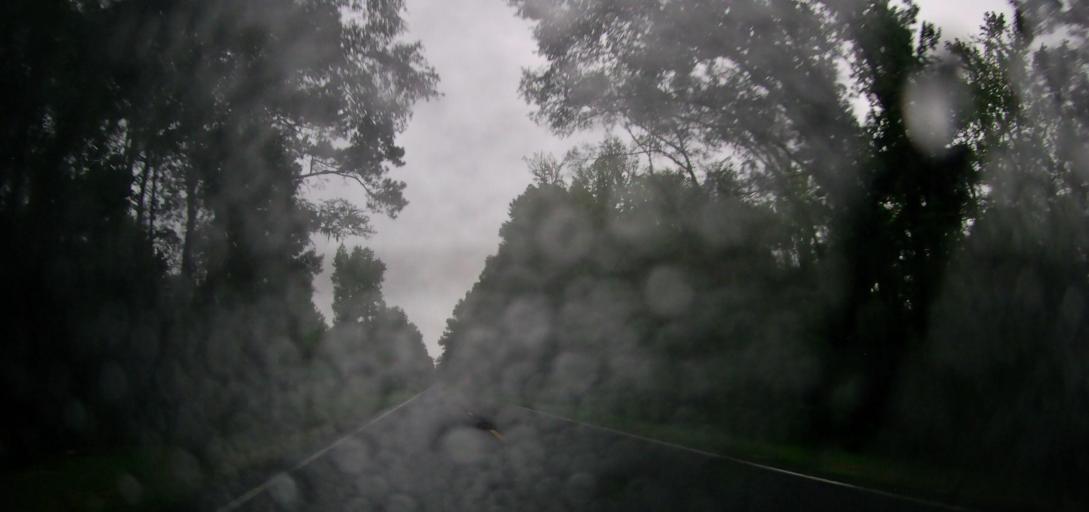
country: US
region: Georgia
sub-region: Glynn County
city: Dock Junction
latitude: 31.2839
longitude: -81.6716
